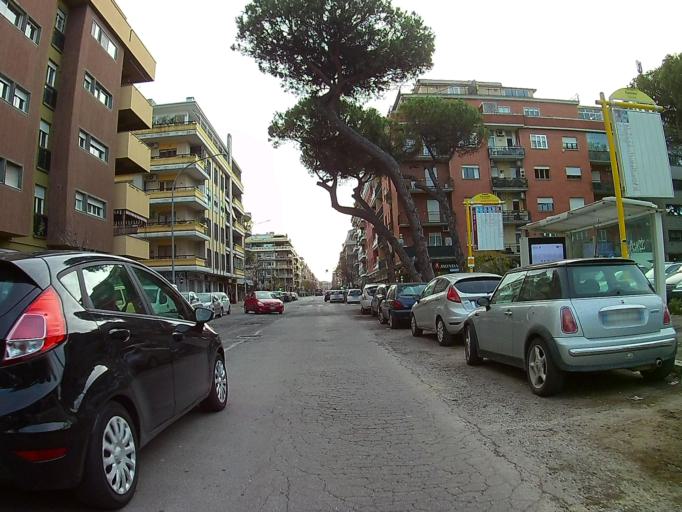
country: IT
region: Latium
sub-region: Citta metropolitana di Roma Capitale
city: Lido di Ostia
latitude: 41.7395
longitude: 12.2802
